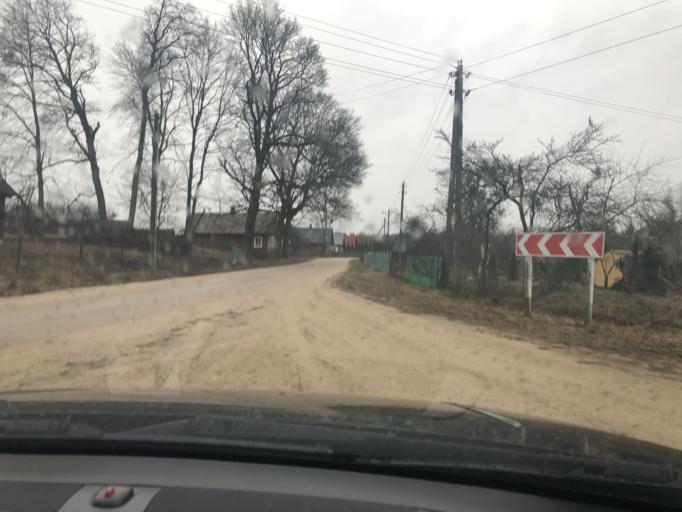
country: BY
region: Grodnenskaya
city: Skidal'
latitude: 53.8565
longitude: 24.2521
